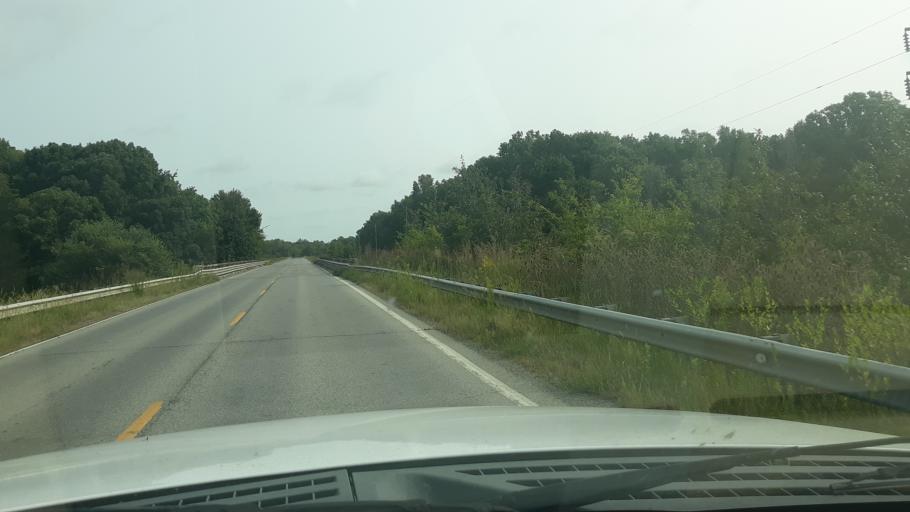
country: US
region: Illinois
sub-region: Saline County
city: Eldorado
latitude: 37.8836
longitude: -88.3886
